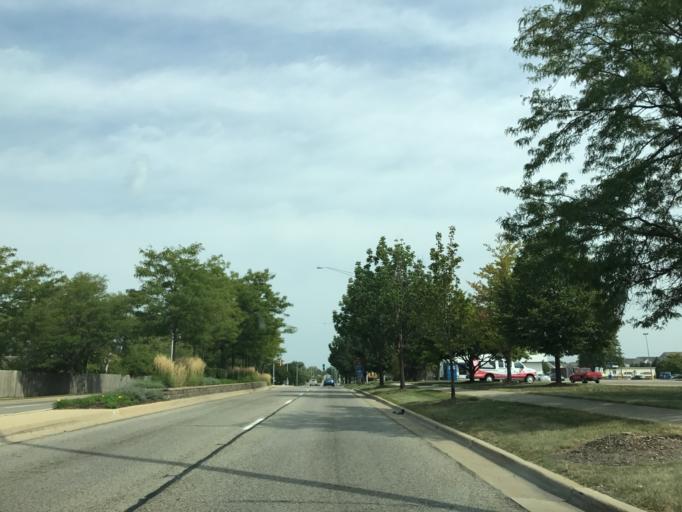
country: US
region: Illinois
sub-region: Will County
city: Bolingbrook
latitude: 41.6966
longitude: -88.0681
